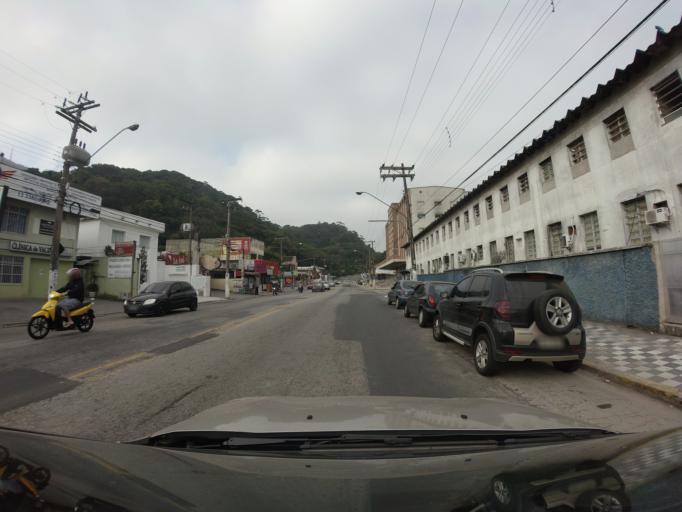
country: BR
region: Sao Paulo
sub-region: Guaruja
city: Guaruja
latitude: -23.9903
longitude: -46.2536
